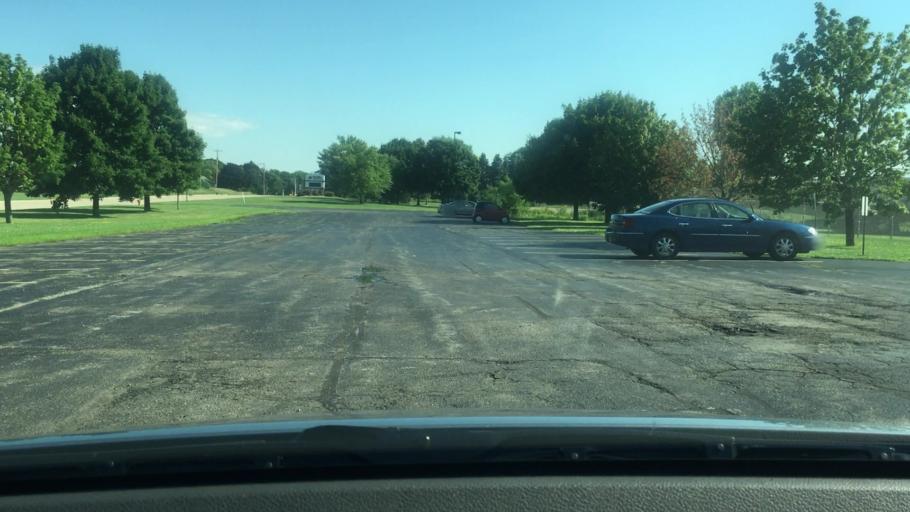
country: US
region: Wisconsin
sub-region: Winnebago County
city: Oshkosh
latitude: 43.9728
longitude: -88.5435
